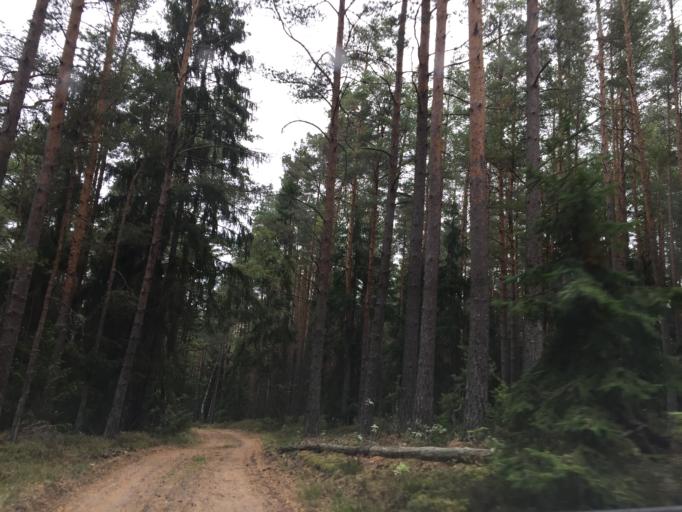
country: LV
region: Salacgrivas
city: Salacgriva
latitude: 57.7060
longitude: 24.3544
